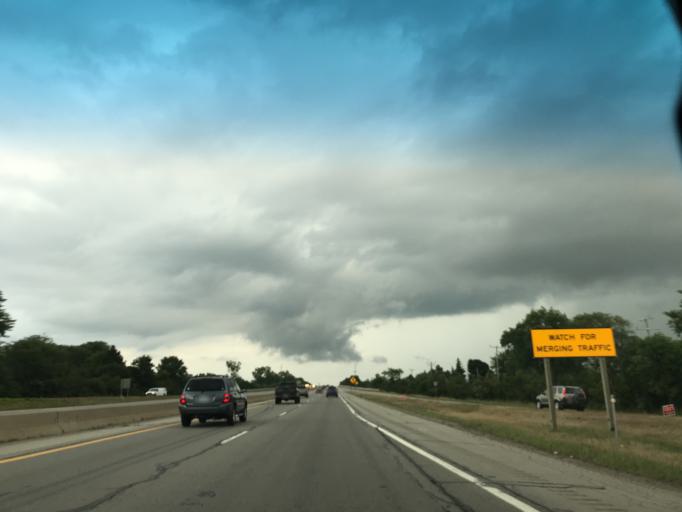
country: US
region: Michigan
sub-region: Washtenaw County
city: Ann Arbor
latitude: 42.2369
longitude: -83.7373
